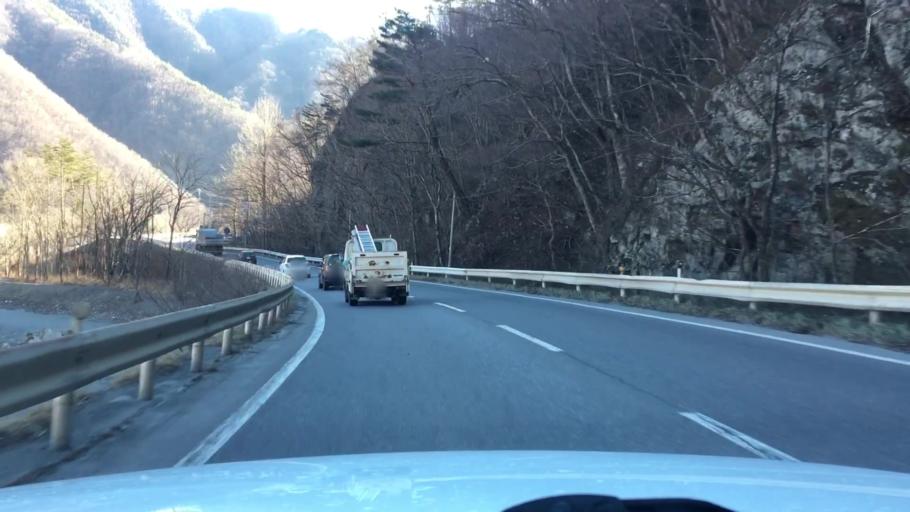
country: JP
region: Iwate
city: Miyako
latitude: 39.6248
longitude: 141.8092
